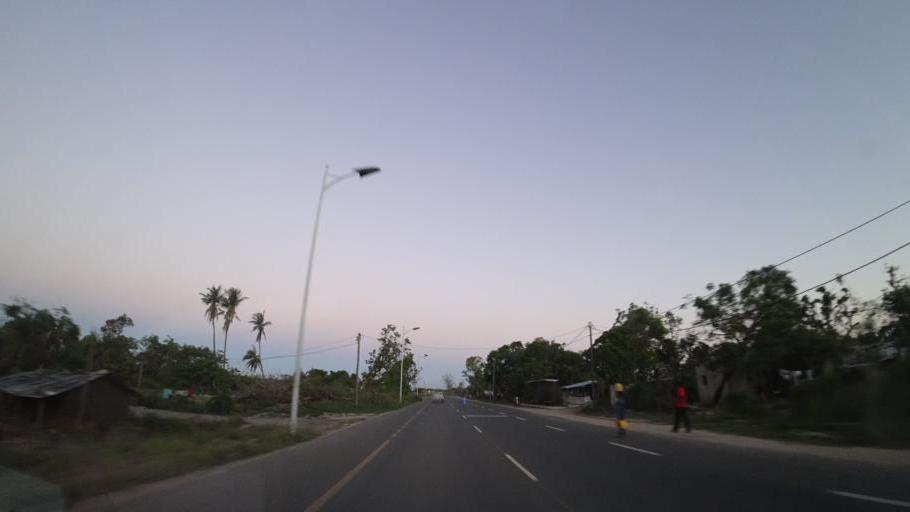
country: MZ
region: Sofala
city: Dondo
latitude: -19.5454
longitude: 34.6426
